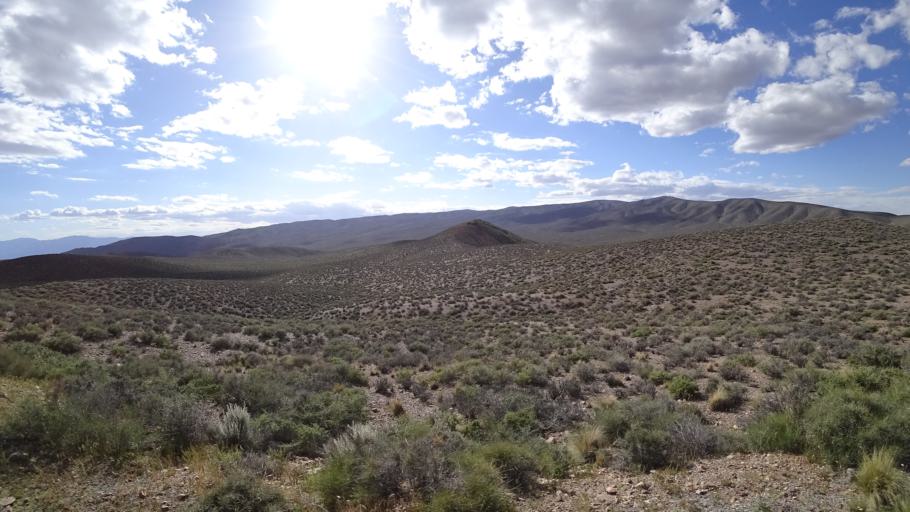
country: US
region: California
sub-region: San Bernardino County
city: Searles Valley
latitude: 36.3197
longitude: -117.1532
